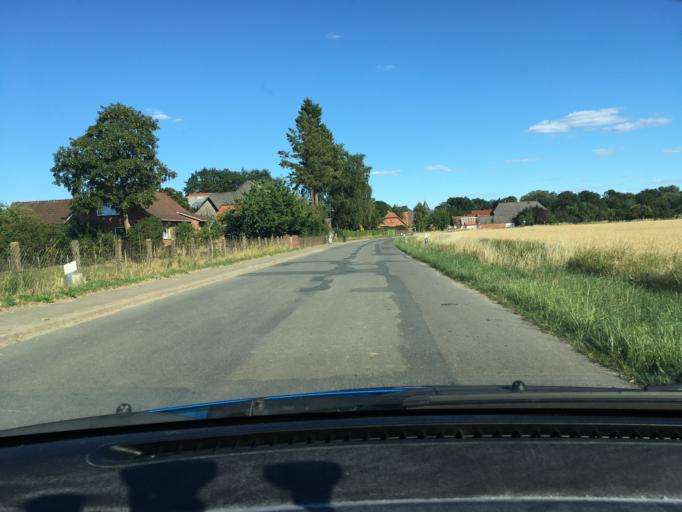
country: DE
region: Mecklenburg-Vorpommern
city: Boizenburg
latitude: 53.3466
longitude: 10.7221
